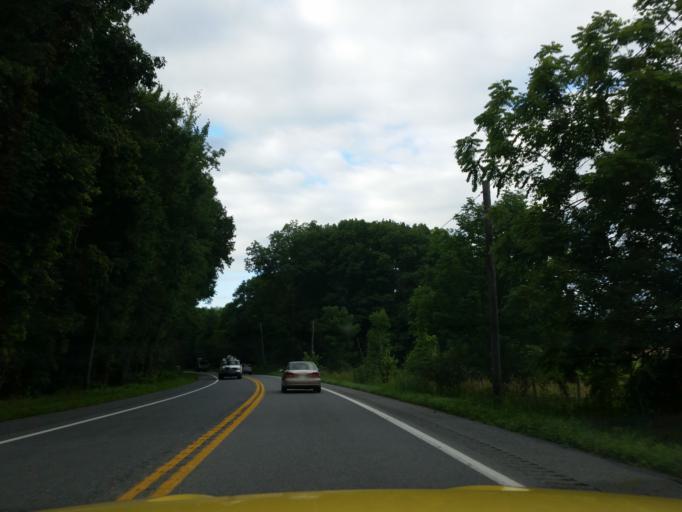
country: US
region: Pennsylvania
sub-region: Lebanon County
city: Campbelltown
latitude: 40.2199
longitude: -76.6189
